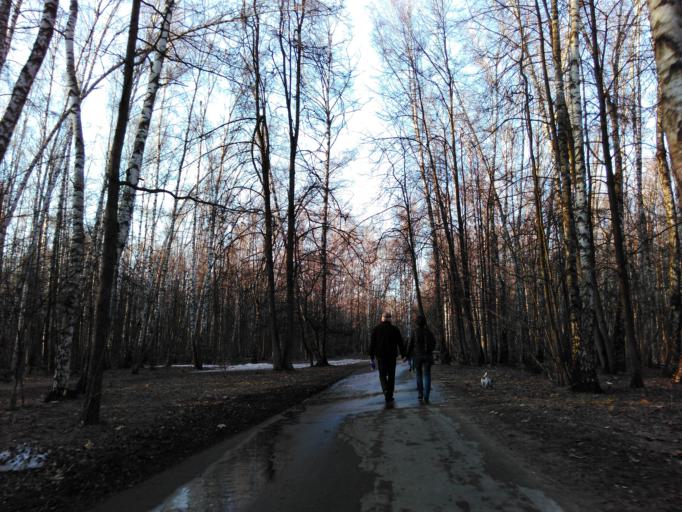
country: RU
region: Moscow
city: Zyuzino
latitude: 55.6433
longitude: 37.5666
